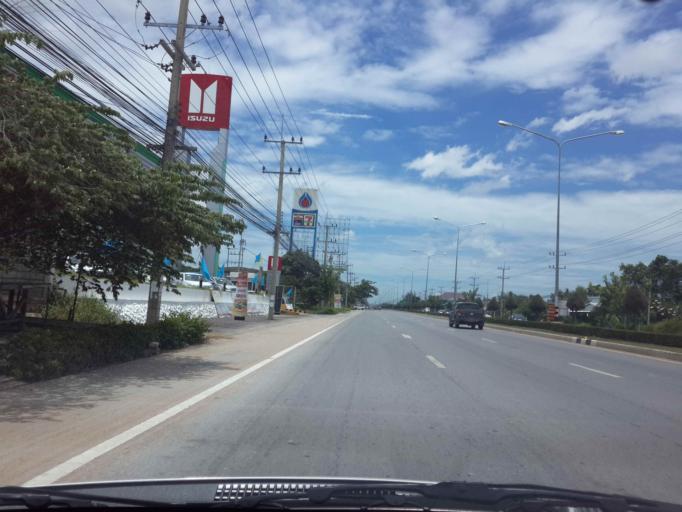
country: TH
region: Prachuap Khiri Khan
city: Hua Hin
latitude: 12.6700
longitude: 99.9523
